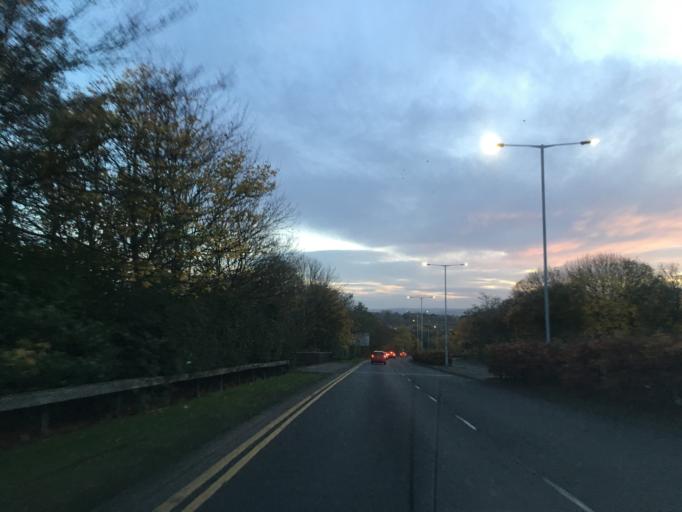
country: GB
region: Scotland
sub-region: Fife
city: Dunfermline
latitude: 56.0706
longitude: -3.4516
